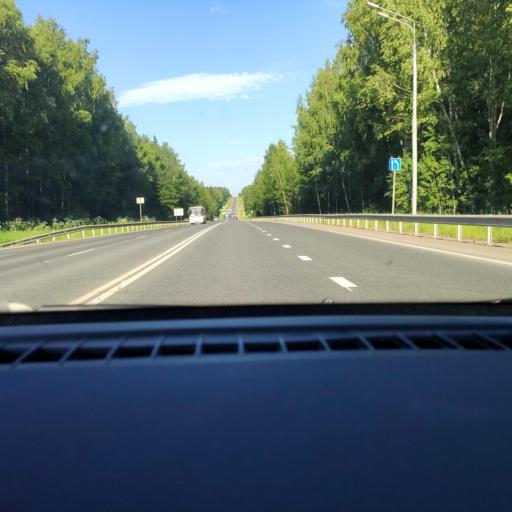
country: RU
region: Udmurtiya
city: Khokhryaki
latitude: 56.9167
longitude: 53.4490
